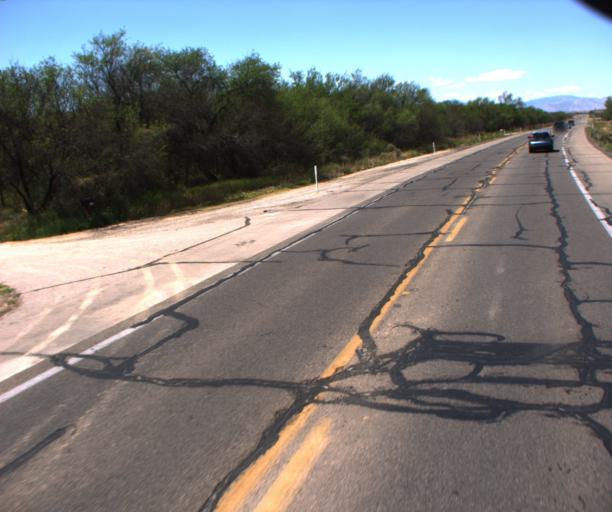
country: US
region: Arizona
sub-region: Cochise County
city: Saint David
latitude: 31.9081
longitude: -110.2562
